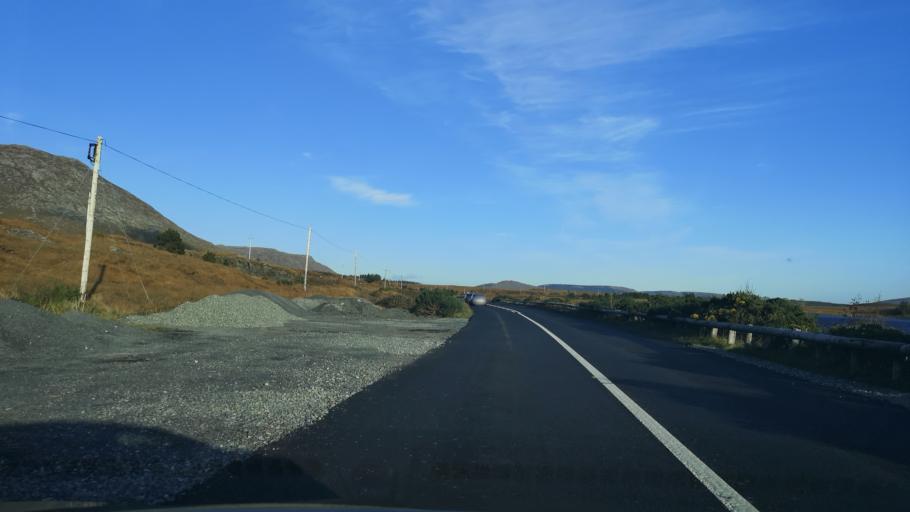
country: IE
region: Connaught
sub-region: County Galway
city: Oughterard
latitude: 53.4555
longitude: -9.6089
